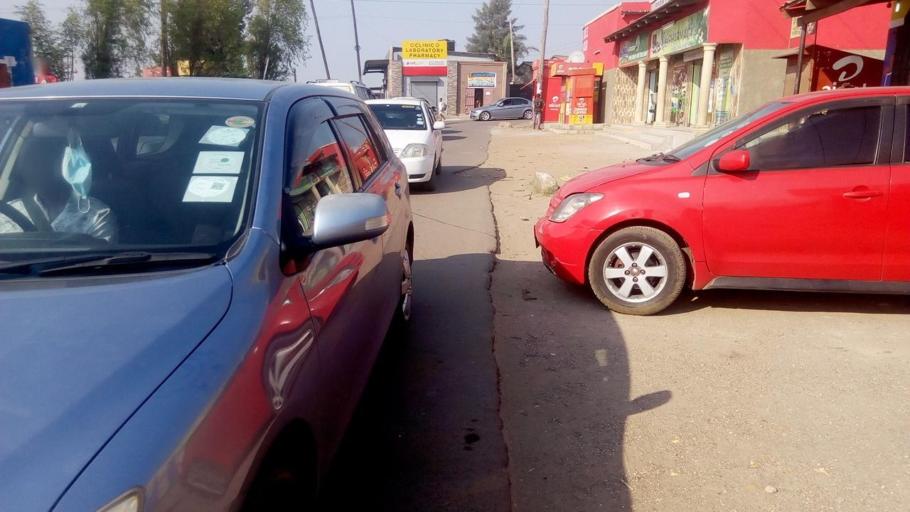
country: ZM
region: Lusaka
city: Lusaka
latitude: -15.3711
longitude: 28.2941
